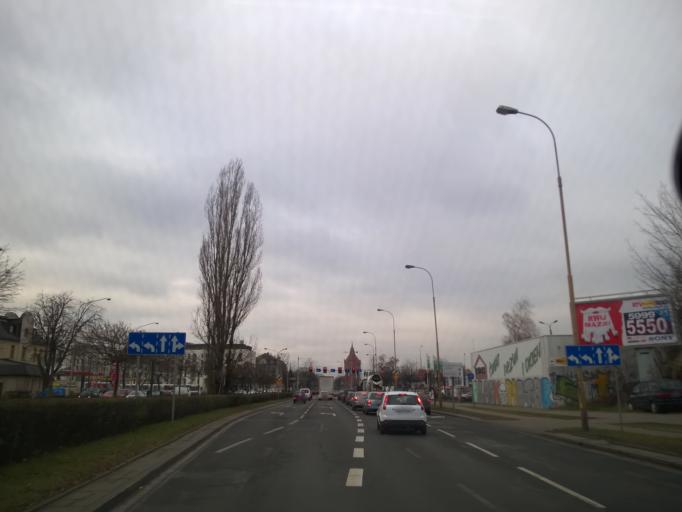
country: PL
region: Lower Silesian Voivodeship
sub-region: Powiat wroclawski
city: Wroclaw
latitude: 51.0838
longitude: 17.0269
